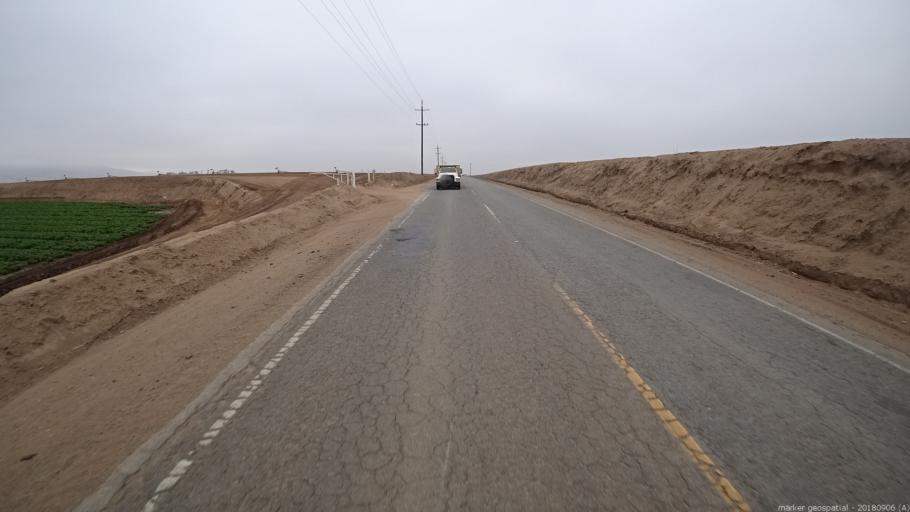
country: US
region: California
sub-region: Monterey County
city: Salinas
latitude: 36.6589
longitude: -121.5888
